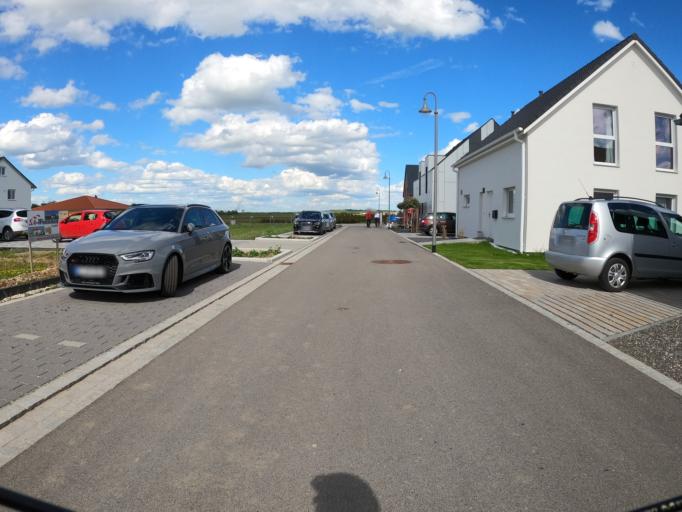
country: DE
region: Bavaria
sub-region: Swabia
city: Leipheim
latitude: 48.4502
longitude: 10.2346
